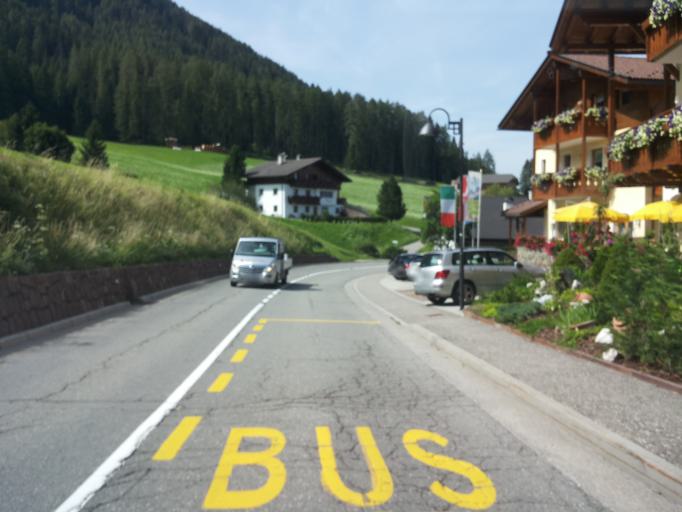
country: IT
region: Trentino-Alto Adige
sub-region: Bolzano
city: Castelrotto
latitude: 46.5751
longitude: 11.5975
